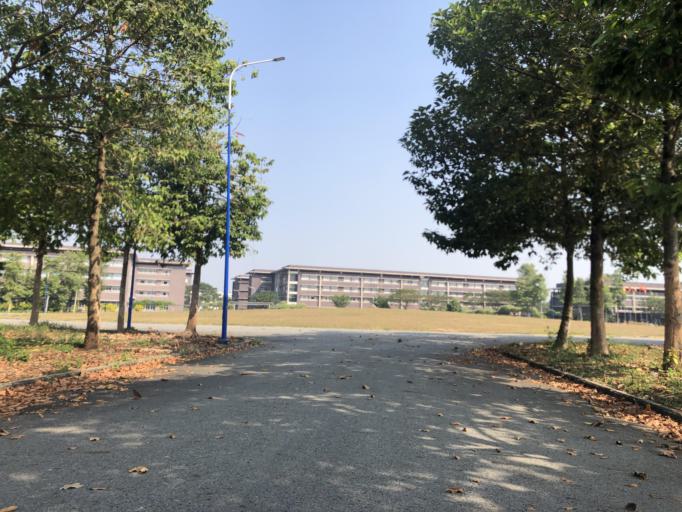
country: VN
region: Binh Duong
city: Thu Dau Mot
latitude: 11.0519
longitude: 106.6659
